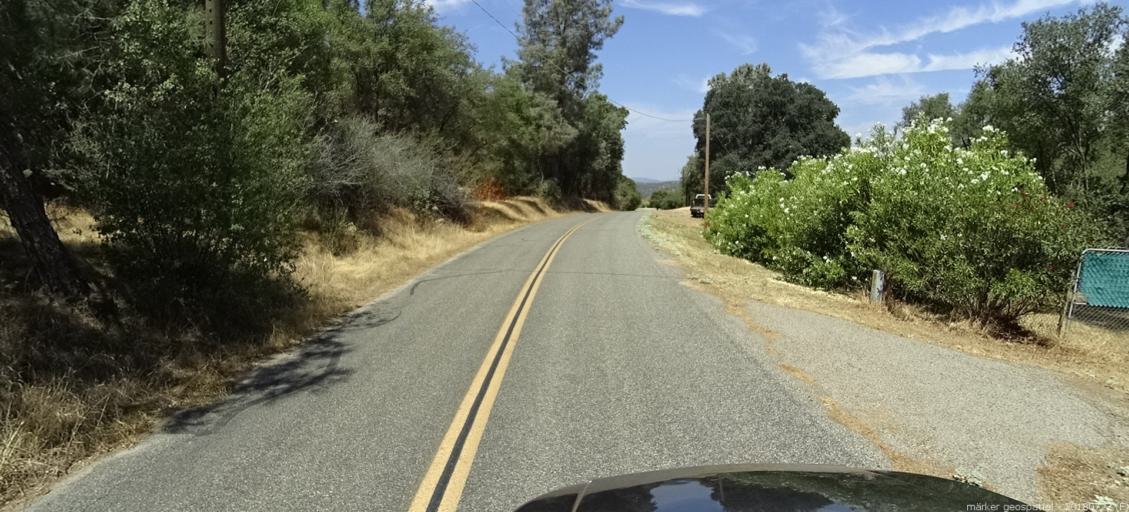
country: US
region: California
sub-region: Madera County
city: Coarsegold
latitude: 37.2775
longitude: -119.7567
